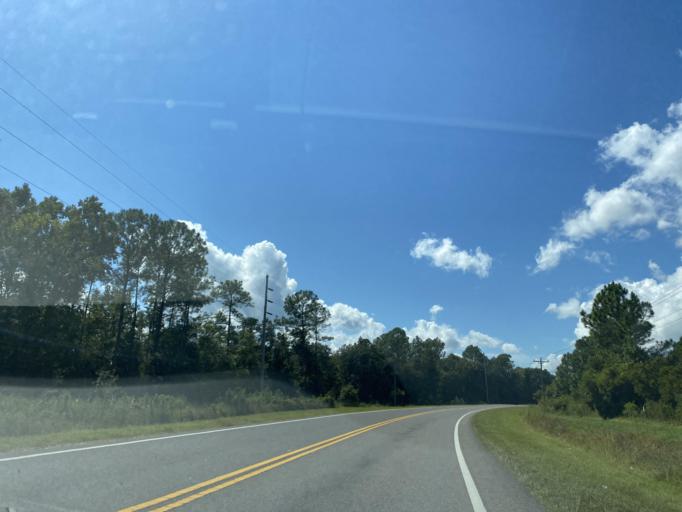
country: US
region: Florida
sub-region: Lake County
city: Umatilla
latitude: 28.9606
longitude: -81.6002
